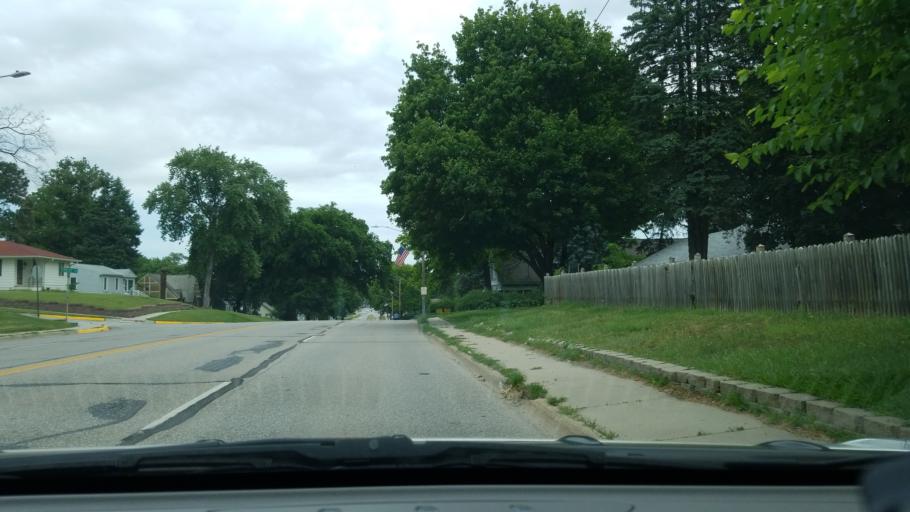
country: US
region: Nebraska
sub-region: Sarpy County
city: Papillion
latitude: 41.1481
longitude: -96.0429
